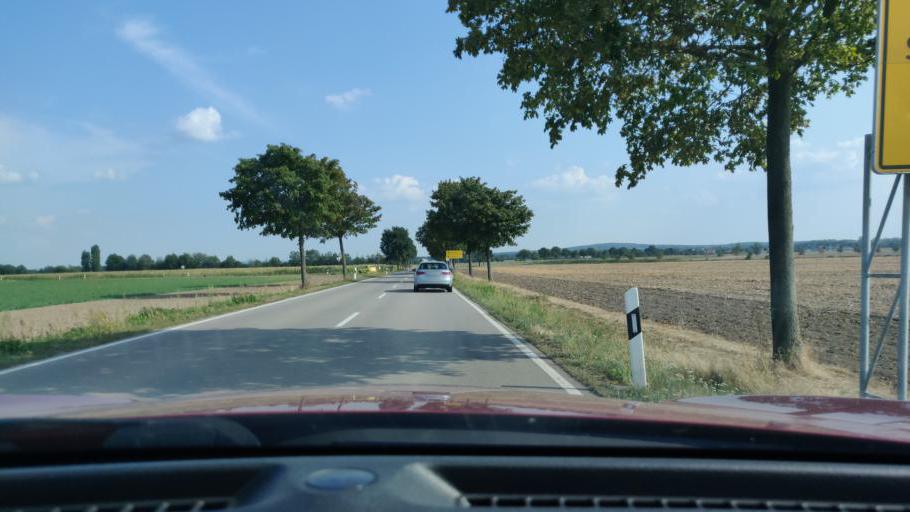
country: DE
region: Saxony
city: Mockrehna
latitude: 51.4895
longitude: 12.8413
